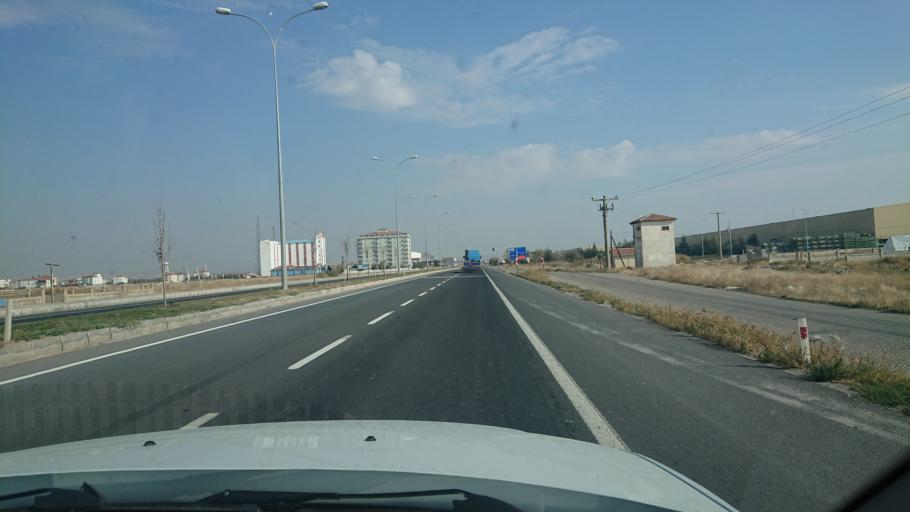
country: TR
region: Aksaray
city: Aksaray
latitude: 38.3484
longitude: 33.9592
